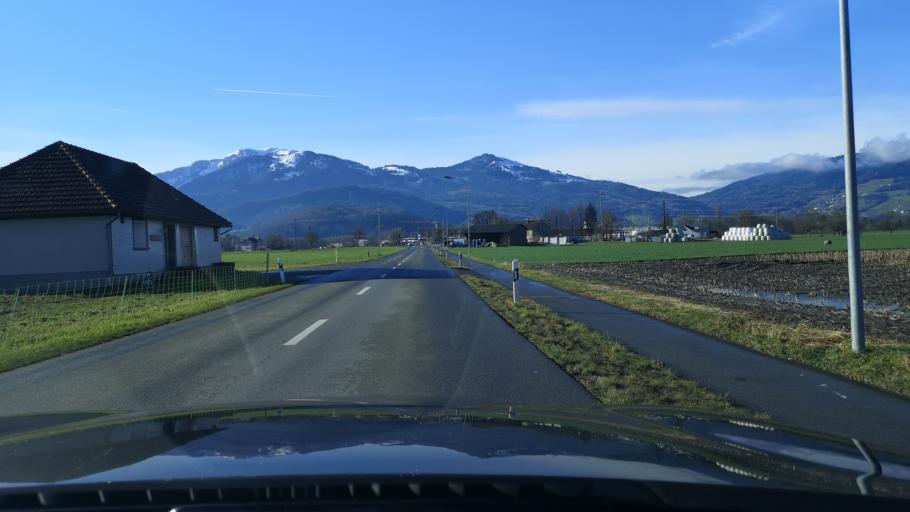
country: AT
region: Vorarlberg
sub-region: Politischer Bezirk Feldkirch
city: Koblach
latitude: 47.3405
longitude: 9.5851
